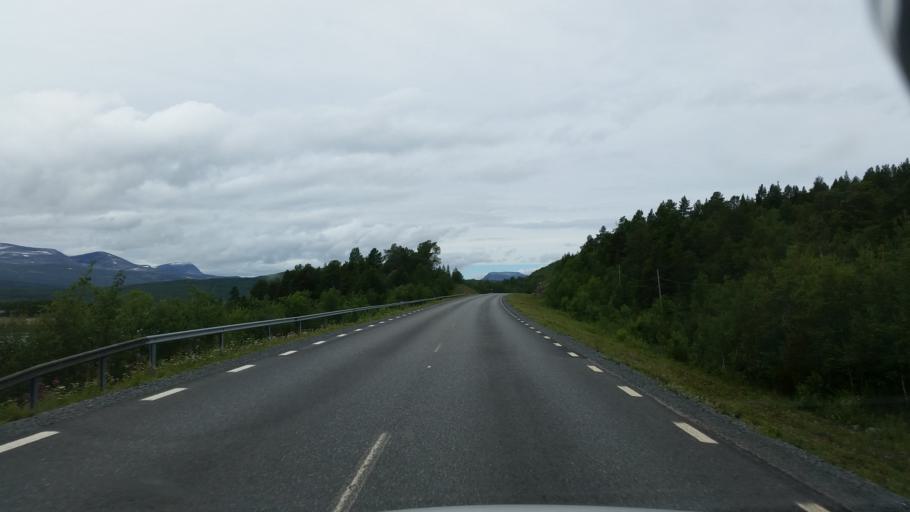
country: NO
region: Nordland
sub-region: Sorfold
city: Straumen
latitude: 66.5215
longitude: 16.3815
